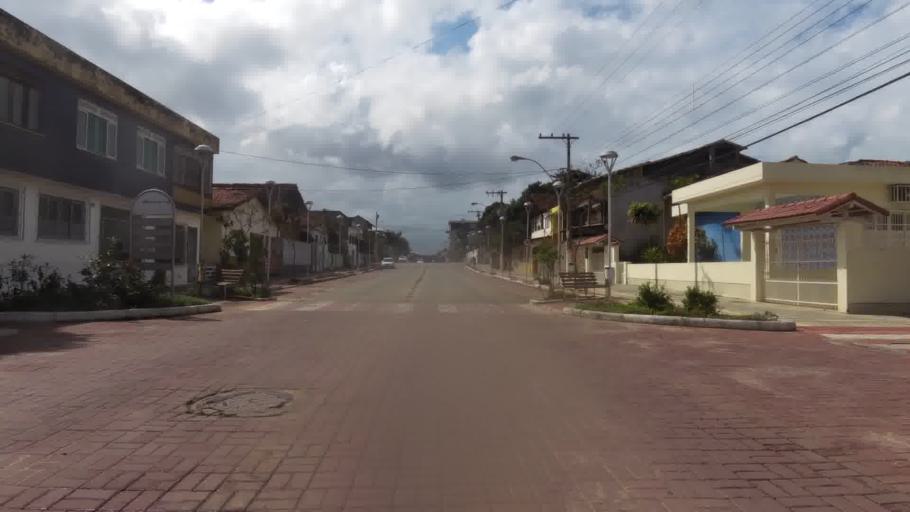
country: BR
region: Espirito Santo
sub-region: Piuma
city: Piuma
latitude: -20.8324
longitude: -40.6970
